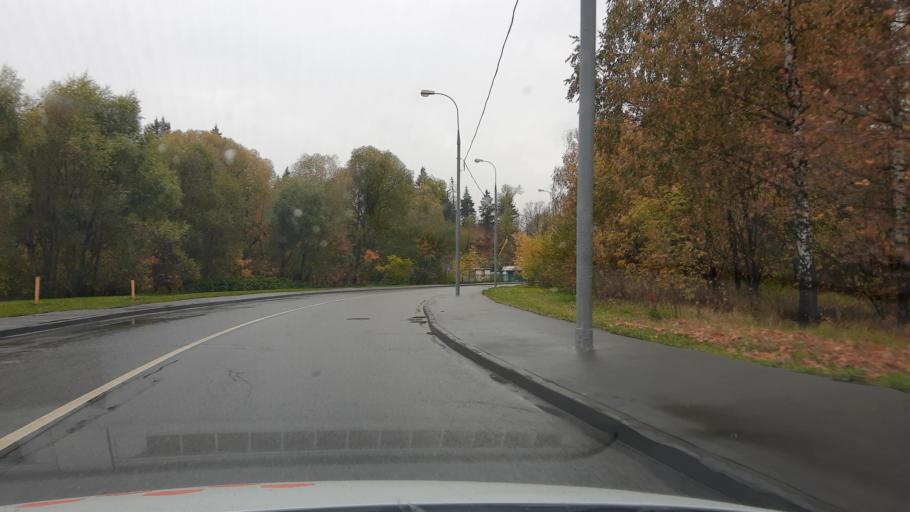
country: RU
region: Moskovskaya
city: Shcherbinka
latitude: 55.5393
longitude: 37.5640
